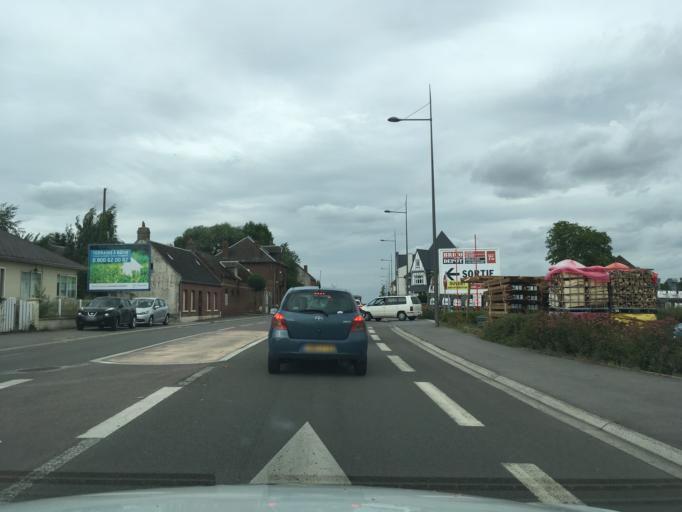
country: FR
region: Nord-Pas-de-Calais
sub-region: Departement du Nord
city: Cambrai
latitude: 50.1544
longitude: 3.2221
